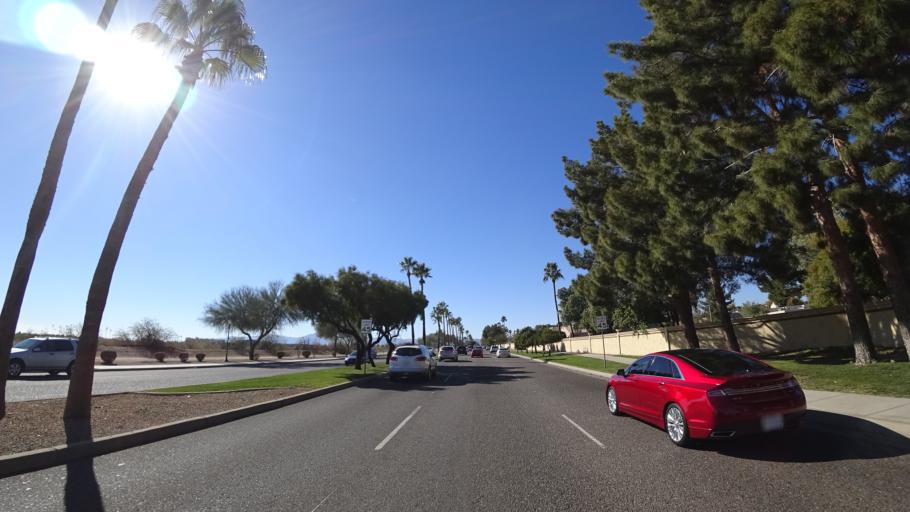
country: US
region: Arizona
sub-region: Maricopa County
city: Sun City West
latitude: 33.6387
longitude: -112.3690
